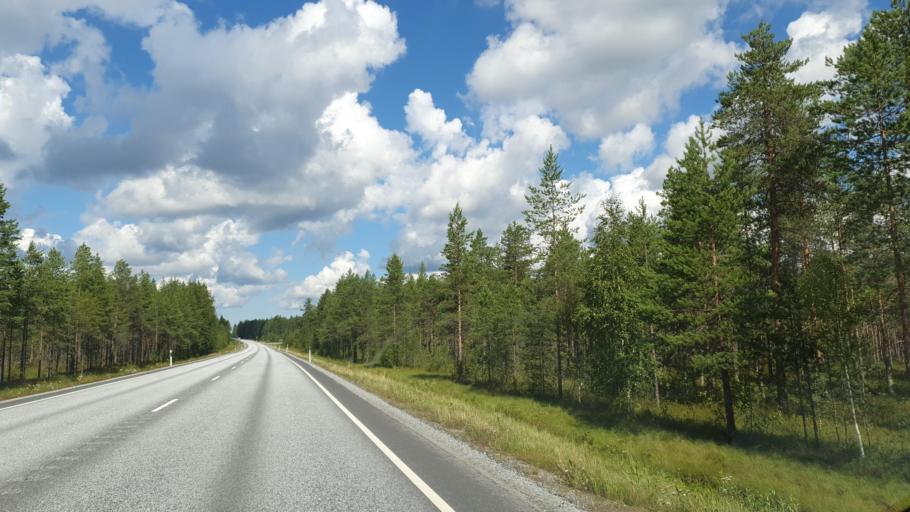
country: FI
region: Northern Savo
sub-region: Ylae-Savo
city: Sonkajaervi
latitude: 63.9242
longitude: 27.3816
